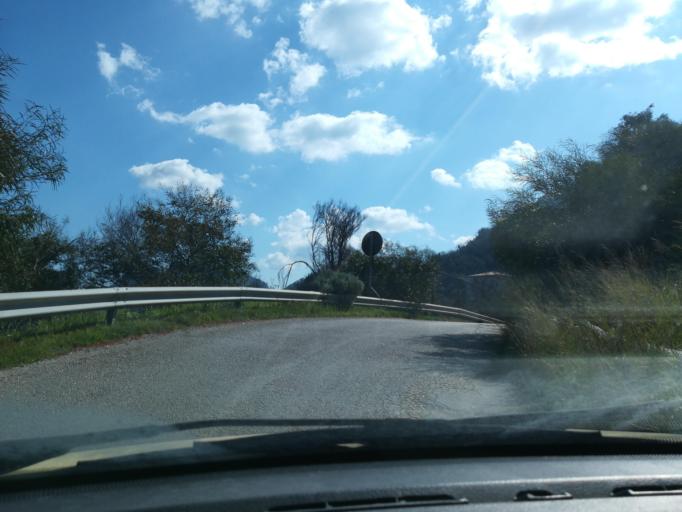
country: IT
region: Sicily
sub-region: Palermo
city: Altofonte
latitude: 38.0442
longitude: 13.2802
